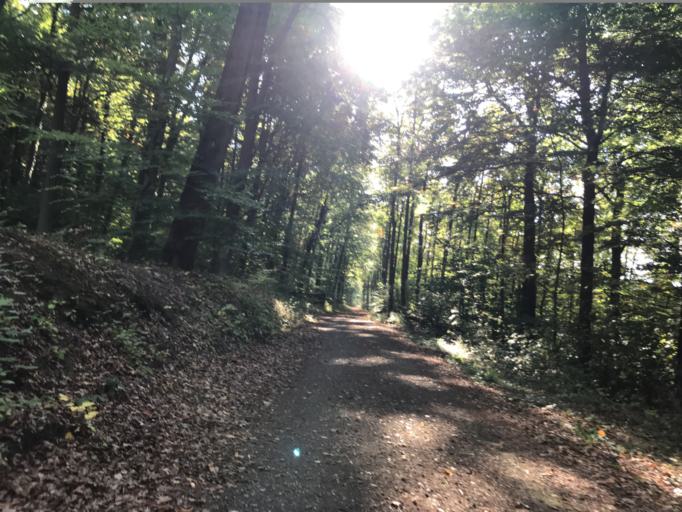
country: DE
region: Rheinland-Pfalz
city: Wolken
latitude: 50.3367
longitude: 7.4488
